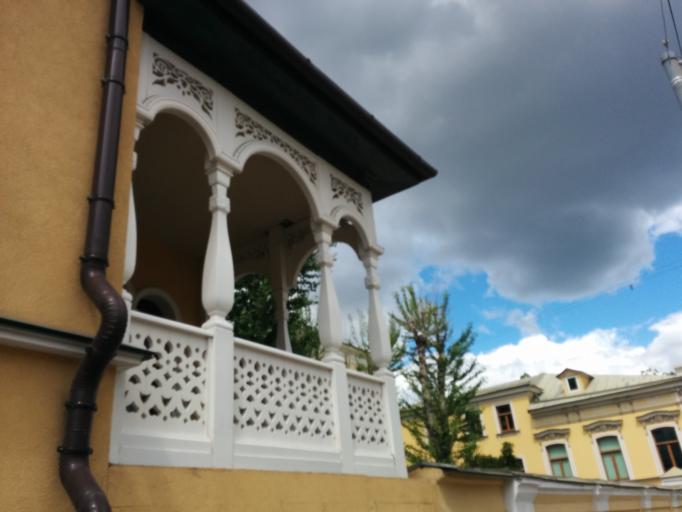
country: RU
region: Moscow
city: Zamoskvorech'ye
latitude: 55.7370
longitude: 37.6243
